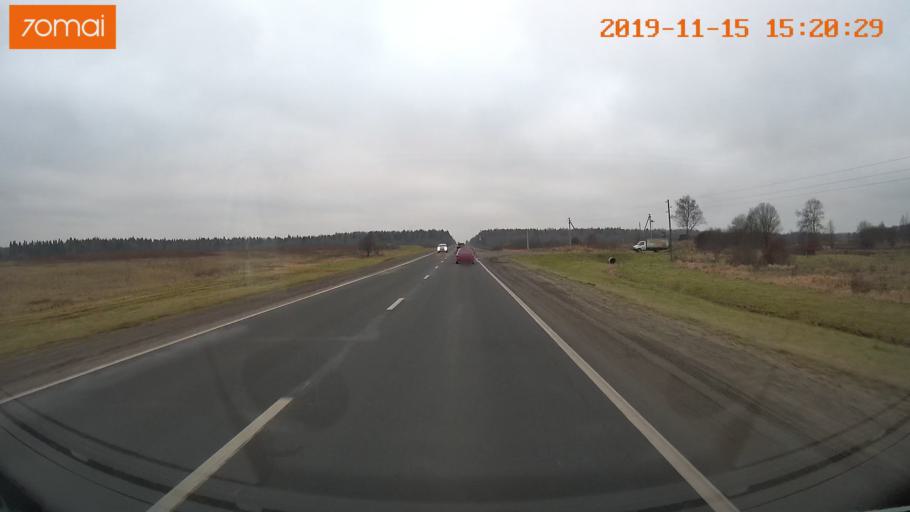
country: RU
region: Jaroslavl
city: Danilov
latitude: 58.2231
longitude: 40.1611
